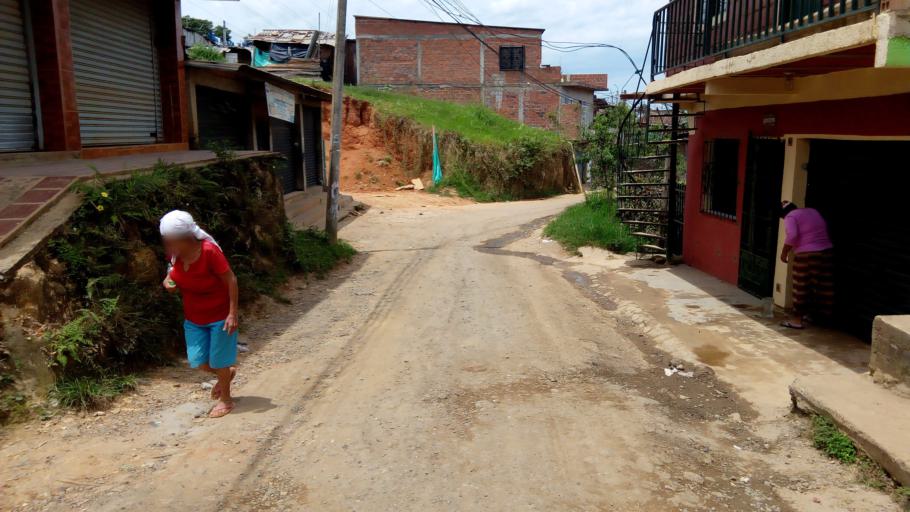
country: CO
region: Valle del Cauca
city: Cali
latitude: 3.3817
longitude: -76.5623
